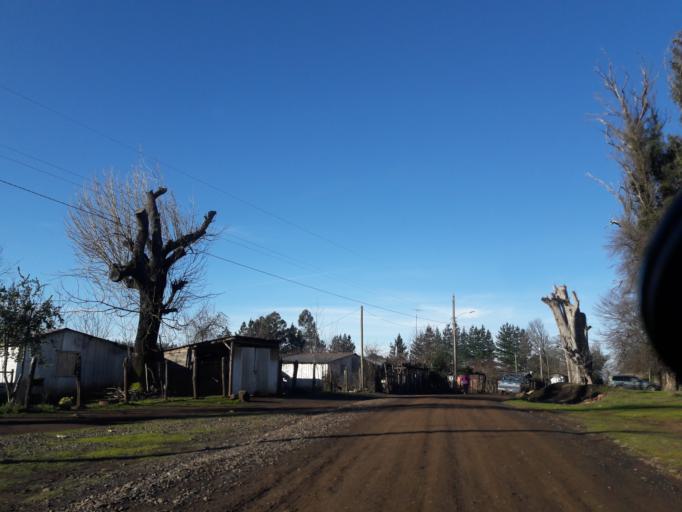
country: CL
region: Biobio
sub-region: Provincia de Biobio
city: Cabrero
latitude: -37.0098
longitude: -72.1836
